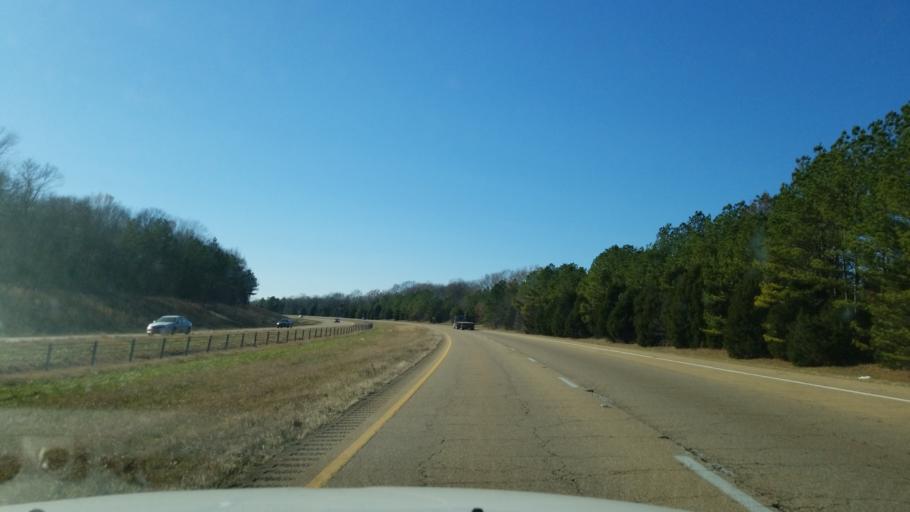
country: US
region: Mississippi
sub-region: Oktibbeha County
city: Starkville
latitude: 33.4846
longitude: -88.7129
